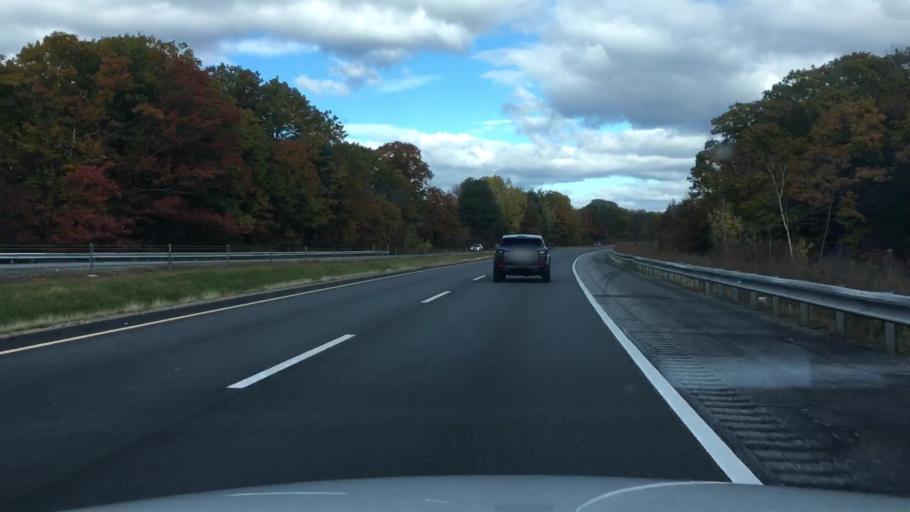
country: US
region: Maine
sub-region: Cumberland County
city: Falmouth
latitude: 43.7099
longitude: -70.2549
